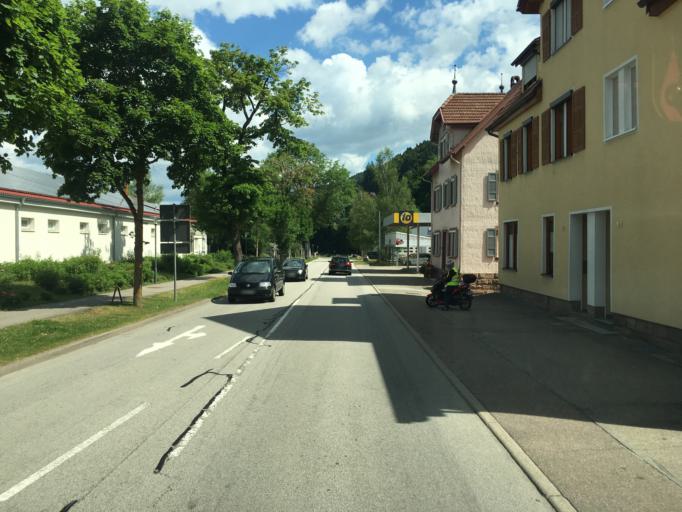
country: DE
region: Baden-Wuerttemberg
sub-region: Karlsruhe Region
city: Baiersbronn
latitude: 48.5281
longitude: 8.4014
